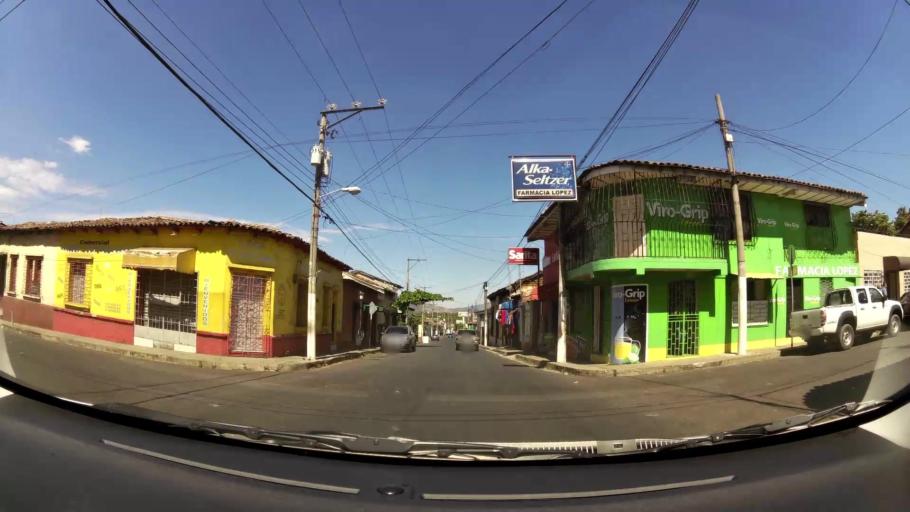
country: SV
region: Ahuachapan
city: Atiquizaya
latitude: 13.9745
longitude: -89.7547
